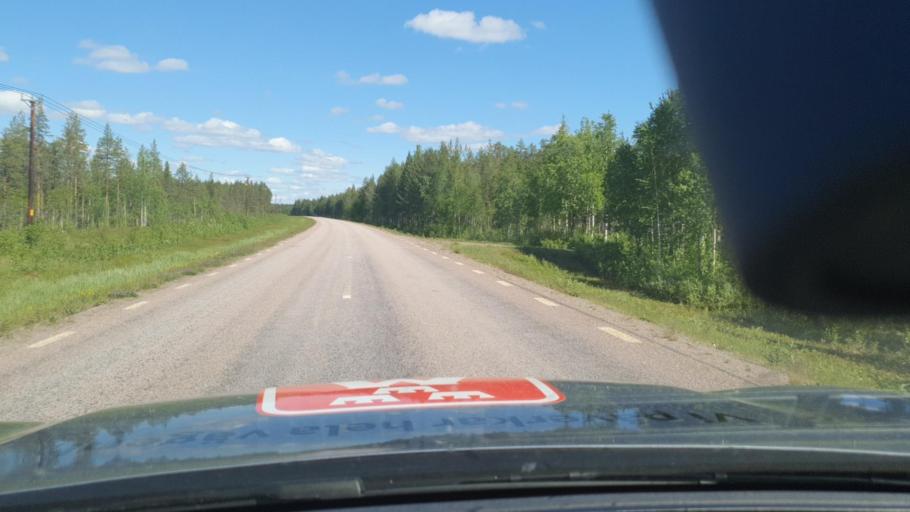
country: SE
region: Norrbotten
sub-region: Pajala Kommun
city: Pajala
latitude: 67.1084
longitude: 22.5993
